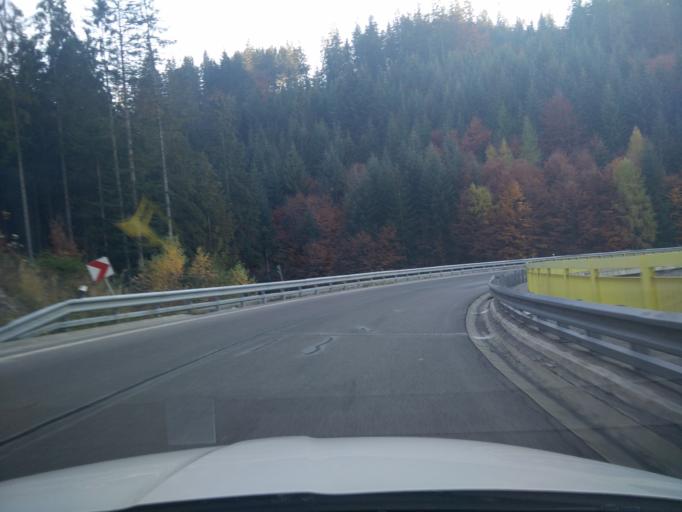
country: PL
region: Silesian Voivodeship
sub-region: Powiat zywiecki
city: Rycerka Gorna
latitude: 49.3713
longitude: 19.0771
